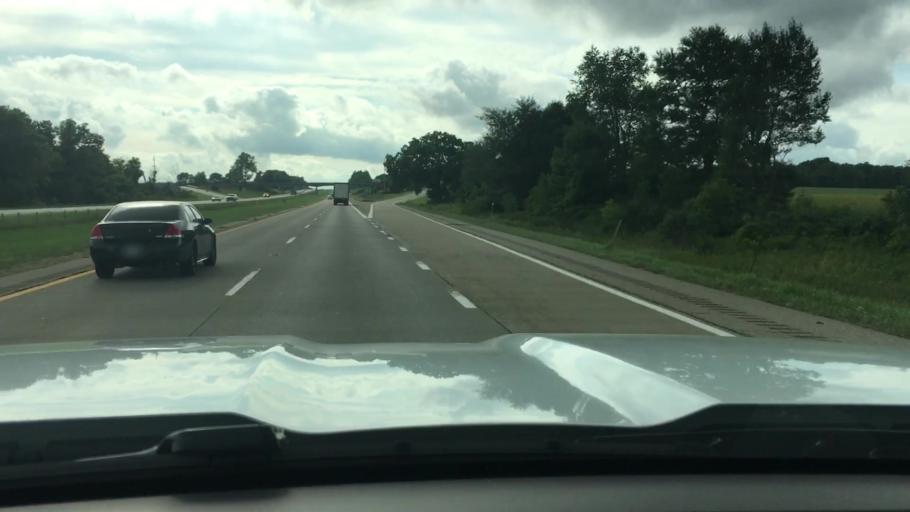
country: US
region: Michigan
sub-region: Ionia County
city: Saranac
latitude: 42.8798
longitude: -85.2354
